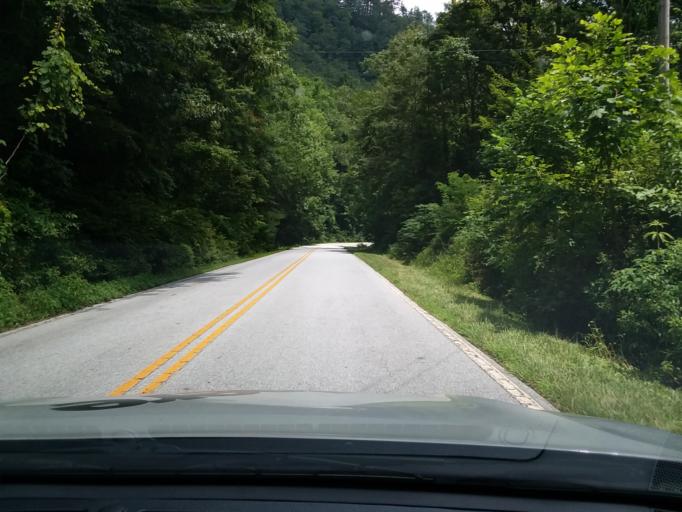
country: US
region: Georgia
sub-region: Rabun County
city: Mountain City
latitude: 35.0285
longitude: -83.1920
